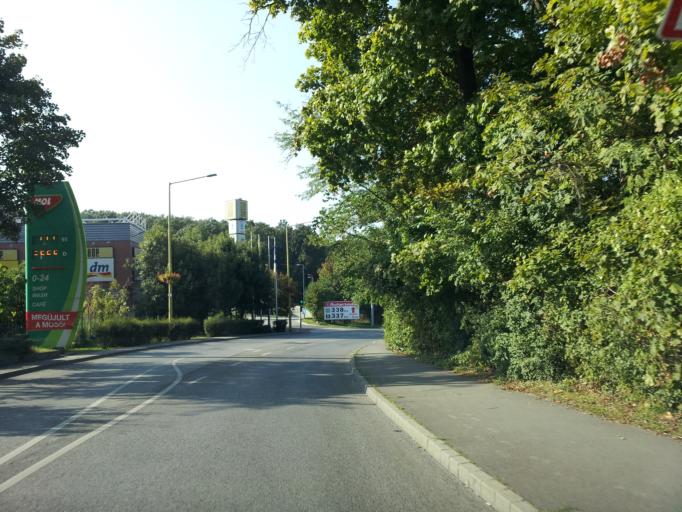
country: HU
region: Pest
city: Budakeszi
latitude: 47.5374
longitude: 18.9677
